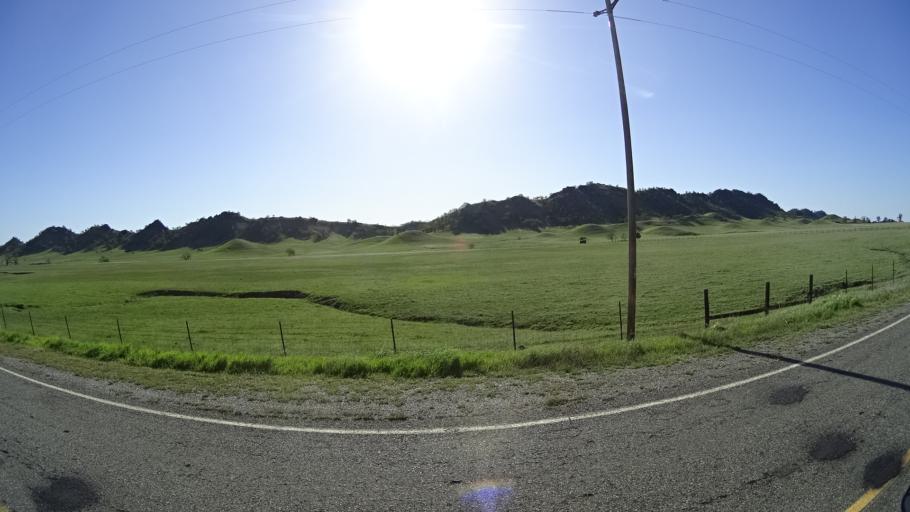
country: US
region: California
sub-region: Tehama County
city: Rancho Tehama Reserve
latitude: 39.7396
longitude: -122.5468
